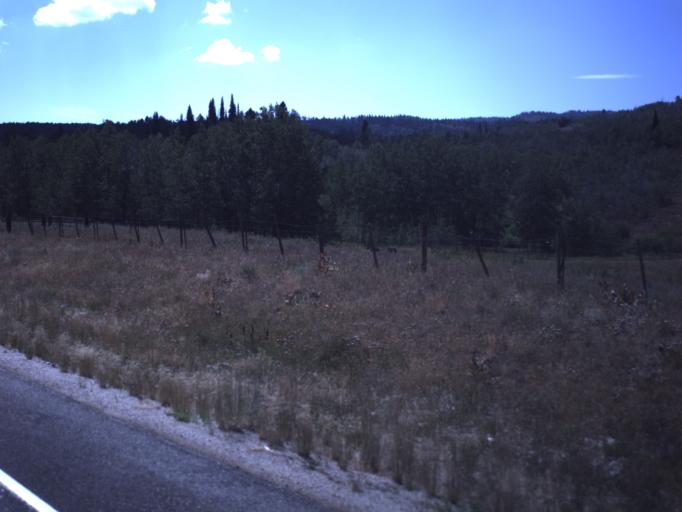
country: US
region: Utah
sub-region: Cache County
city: Richmond
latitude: 41.9194
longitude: -111.5614
